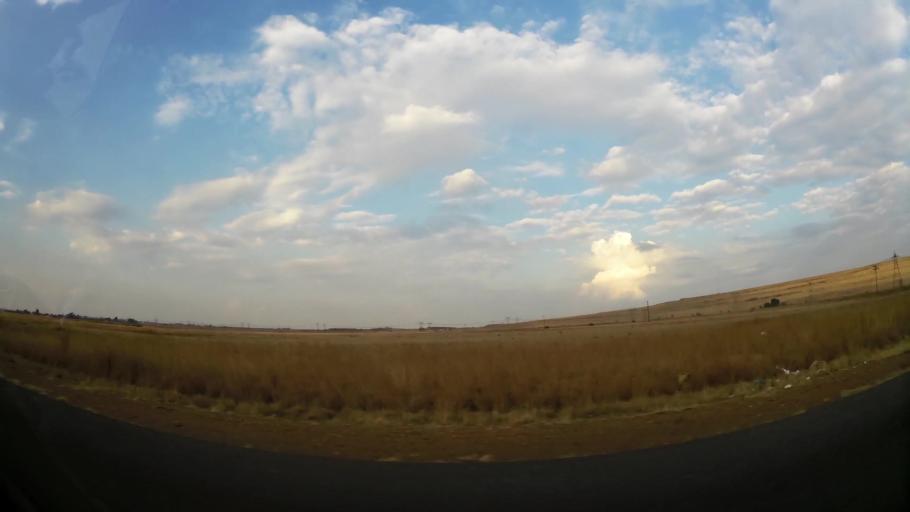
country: ZA
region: Gauteng
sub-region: Sedibeng District Municipality
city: Vanderbijlpark
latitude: -26.6285
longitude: 27.8096
